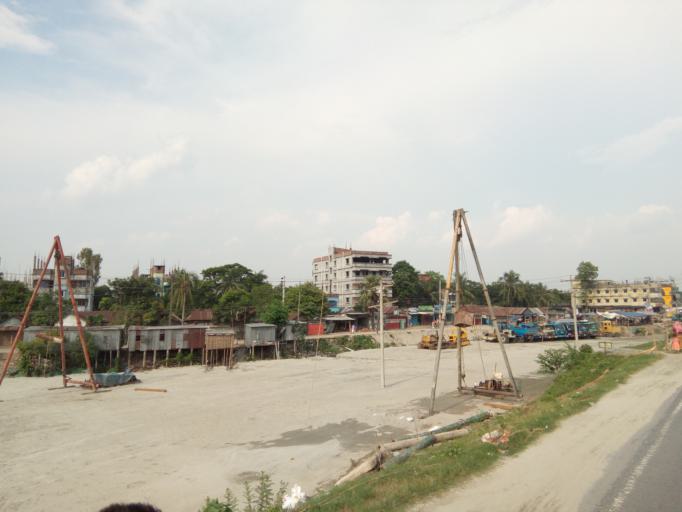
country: BD
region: Dhaka
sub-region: Dhaka
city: Dhaka
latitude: 23.6601
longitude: 90.3579
